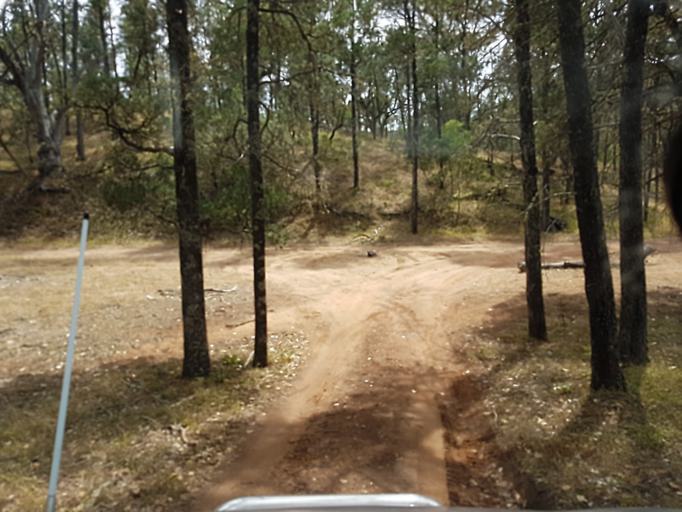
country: AU
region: New South Wales
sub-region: Snowy River
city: Jindabyne
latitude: -36.9443
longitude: 148.3943
